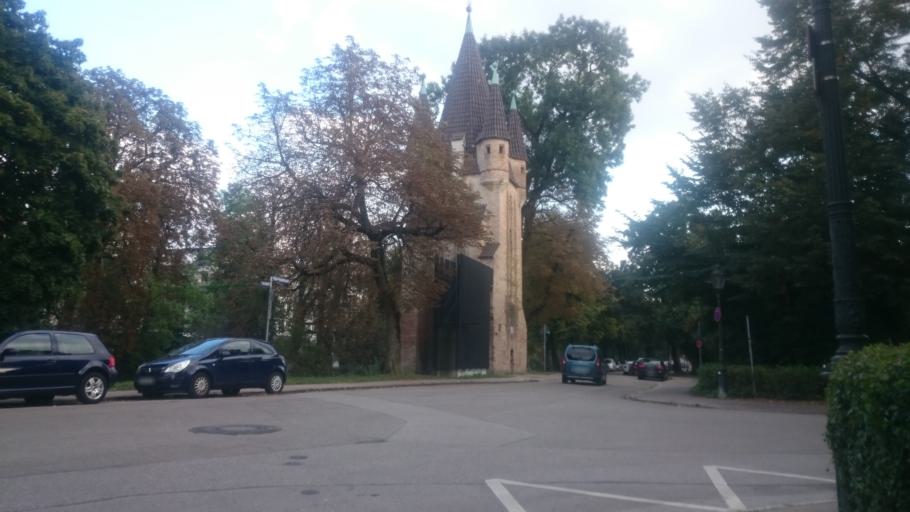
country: DE
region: Bavaria
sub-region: Swabia
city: Augsburg
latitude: 48.3740
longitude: 10.9066
